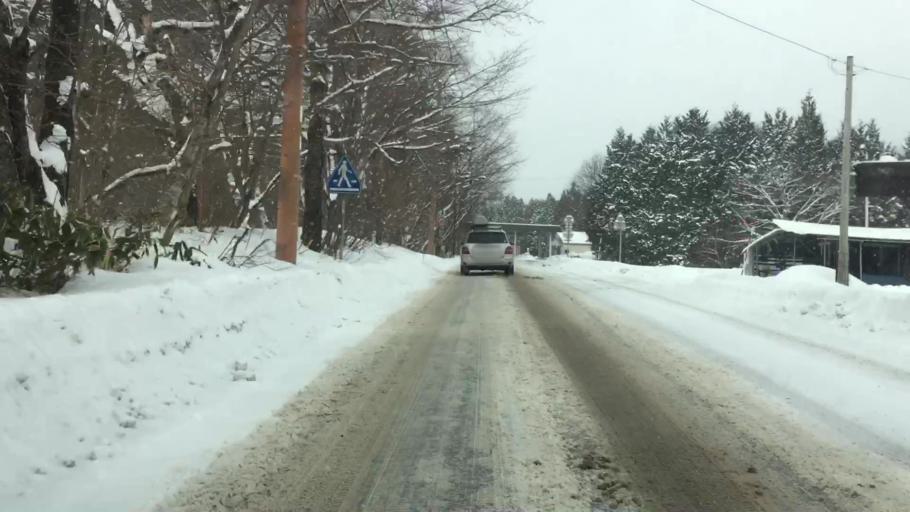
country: JP
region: Tochigi
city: Yaita
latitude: 36.9545
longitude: 139.7694
